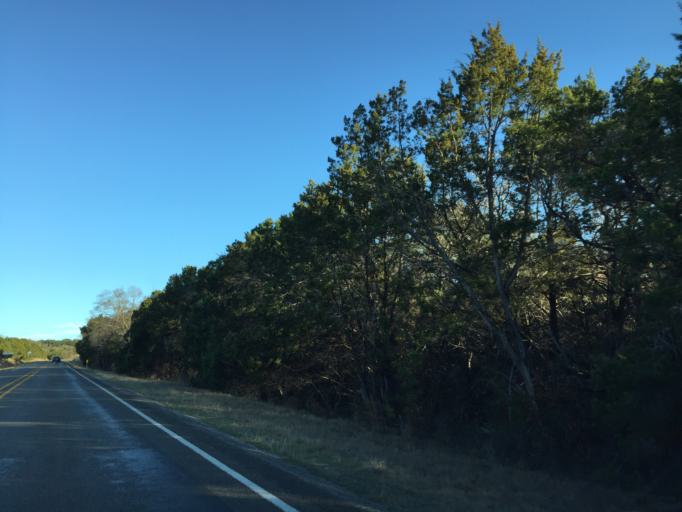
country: US
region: Texas
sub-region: Travis County
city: Lago Vista
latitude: 30.5248
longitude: -98.0875
